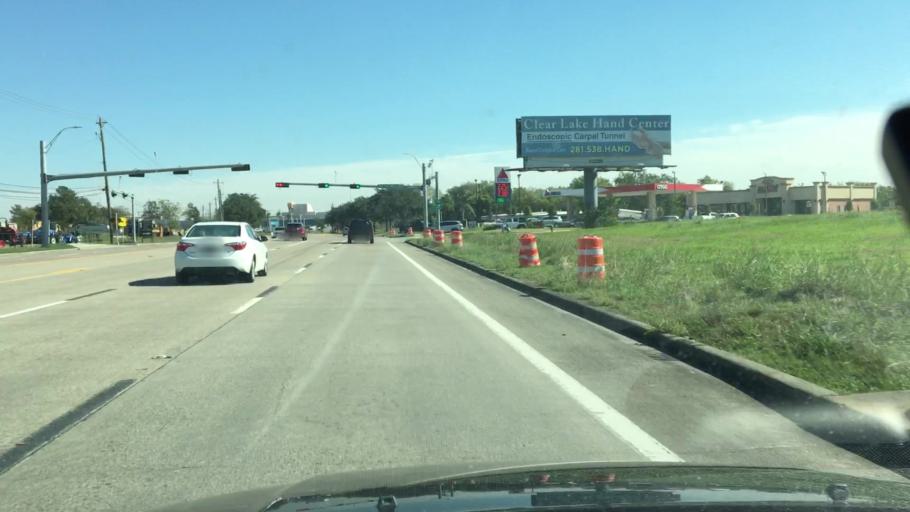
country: US
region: Texas
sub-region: Harris County
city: Webster
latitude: 29.5246
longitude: -95.1391
